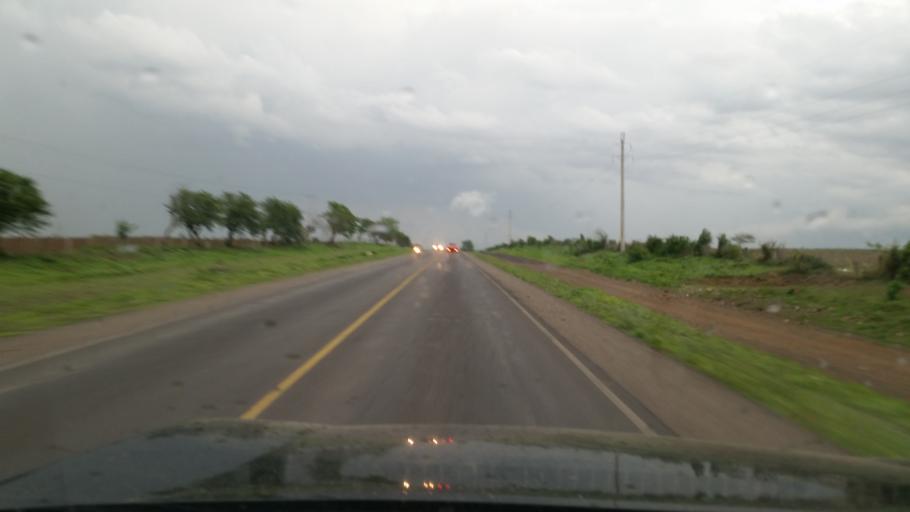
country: NI
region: Chinandega
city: Puerto Morazan
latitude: 12.7908
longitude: -87.0157
